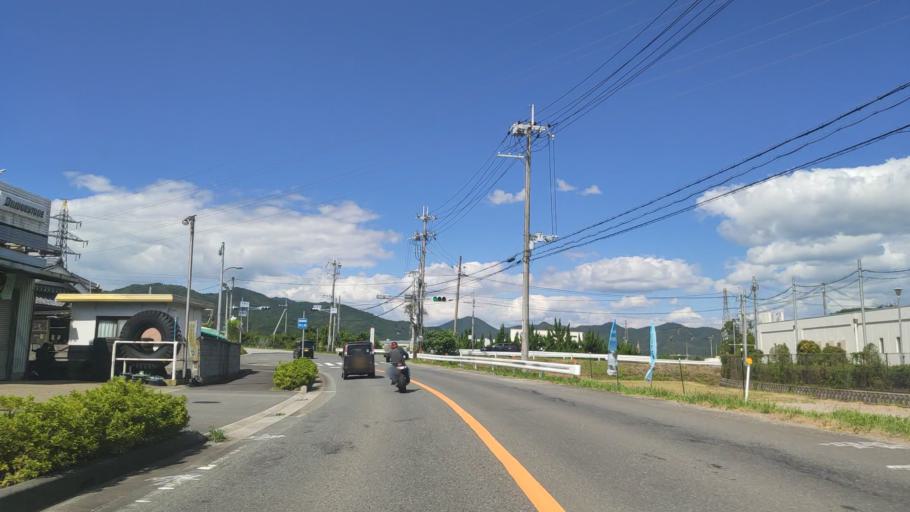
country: JP
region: Kyoto
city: Fukuchiyama
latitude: 35.2155
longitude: 135.1351
